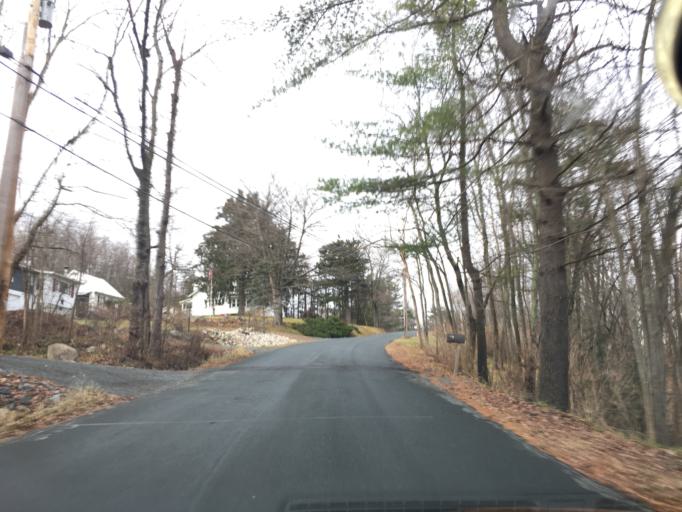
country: US
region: New York
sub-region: Rensselaer County
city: Averill Park
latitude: 42.6049
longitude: -73.5231
